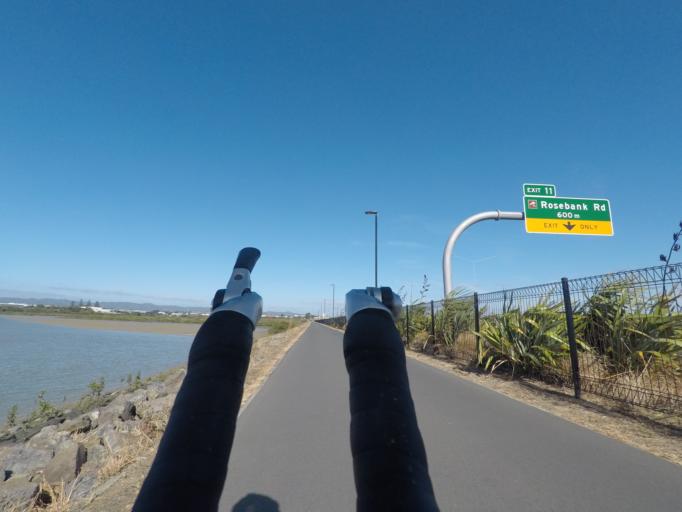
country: NZ
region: Auckland
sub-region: Auckland
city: Rosebank
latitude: -36.8721
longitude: 174.6882
